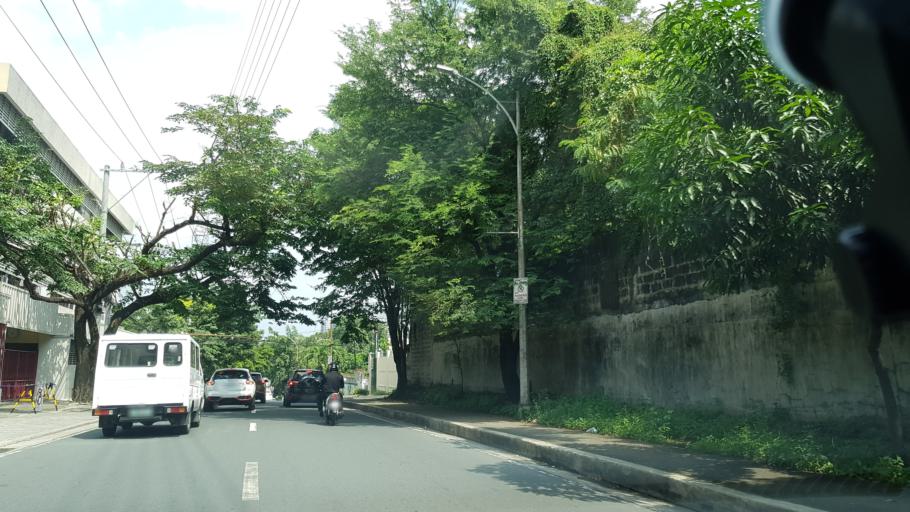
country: PH
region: Metro Manila
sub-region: San Juan
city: San Juan
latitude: 14.6159
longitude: 121.0364
